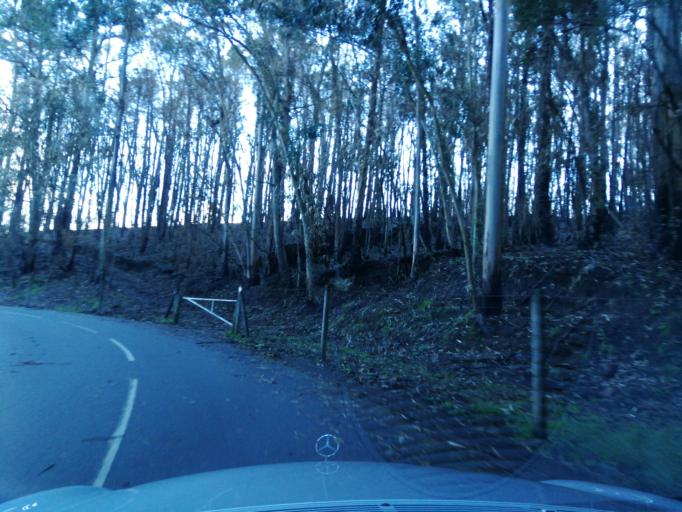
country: PT
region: Braga
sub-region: Braga
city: Braga
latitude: 41.5393
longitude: -8.3897
